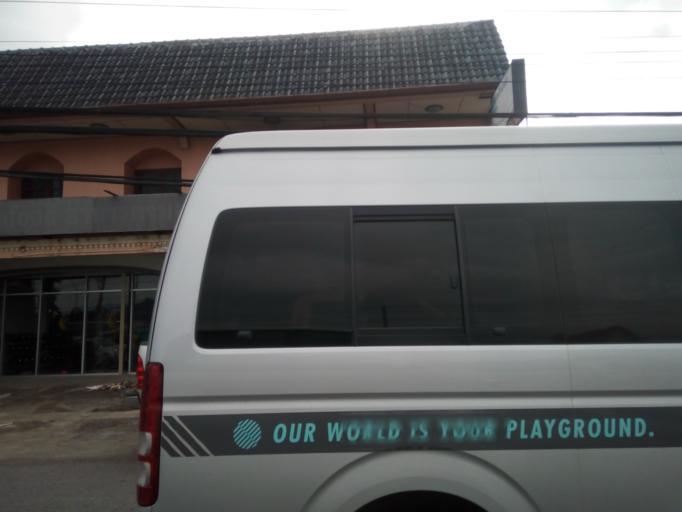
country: TH
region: Phuket
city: Thalang
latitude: 8.0062
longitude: 98.3430
